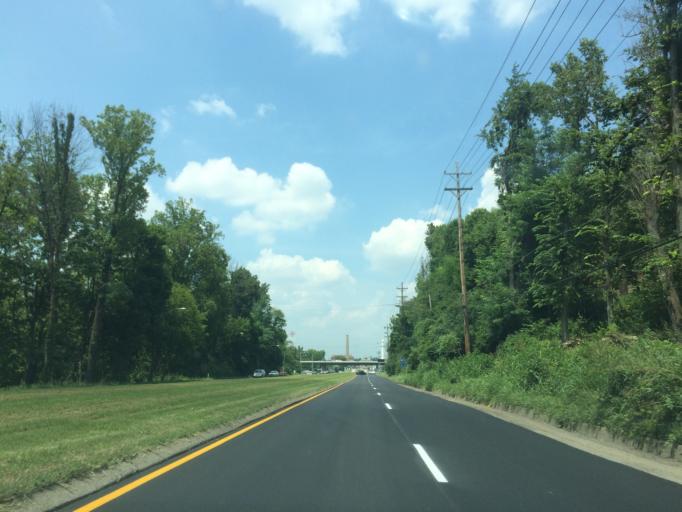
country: US
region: Kentucky
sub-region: Jefferson County
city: Indian Hills
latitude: 38.2718
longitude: -85.6947
